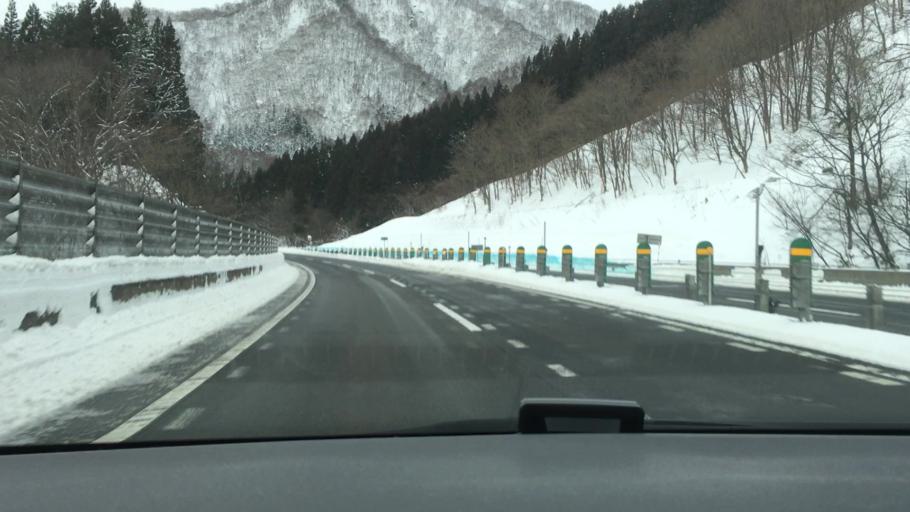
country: JP
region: Akita
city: Hanawa
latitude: 40.1316
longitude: 140.9194
